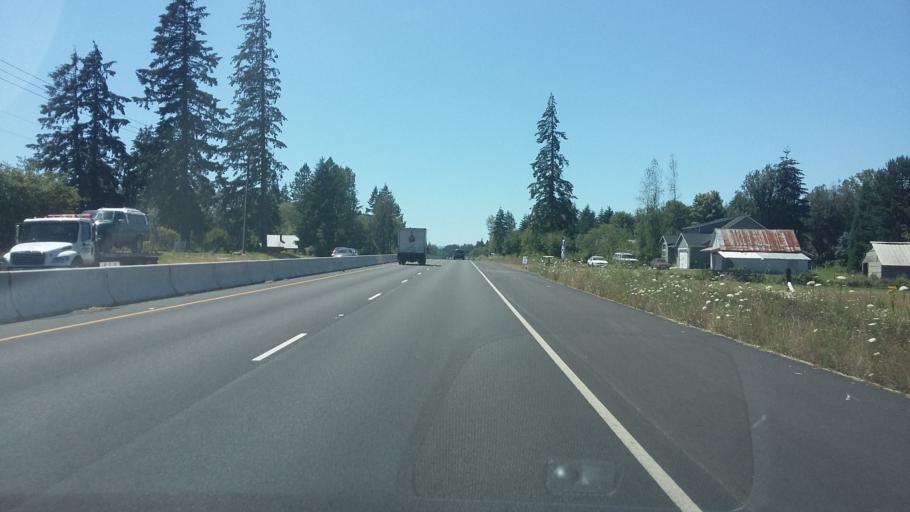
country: US
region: Washington
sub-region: Clark County
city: Dollar Corner
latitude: 45.7798
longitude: -122.6453
